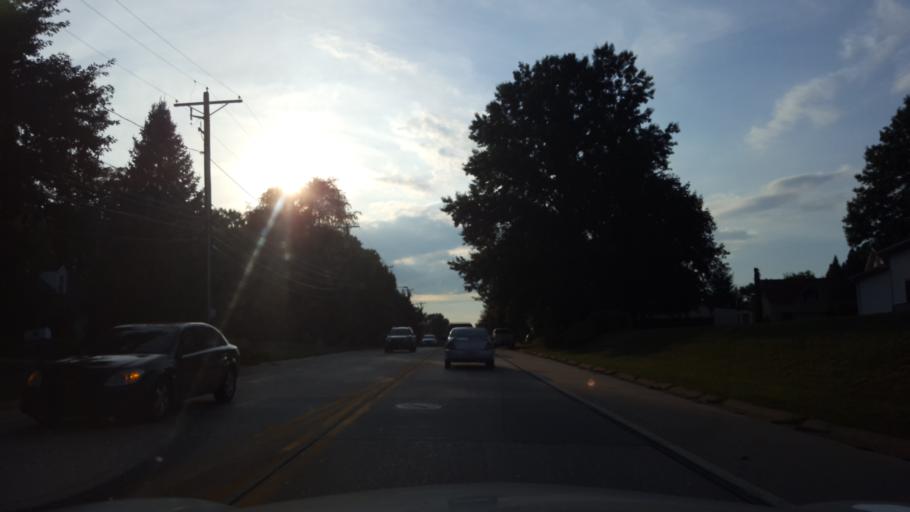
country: US
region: Delaware
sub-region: New Castle County
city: Newport
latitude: 39.7404
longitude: -75.6394
